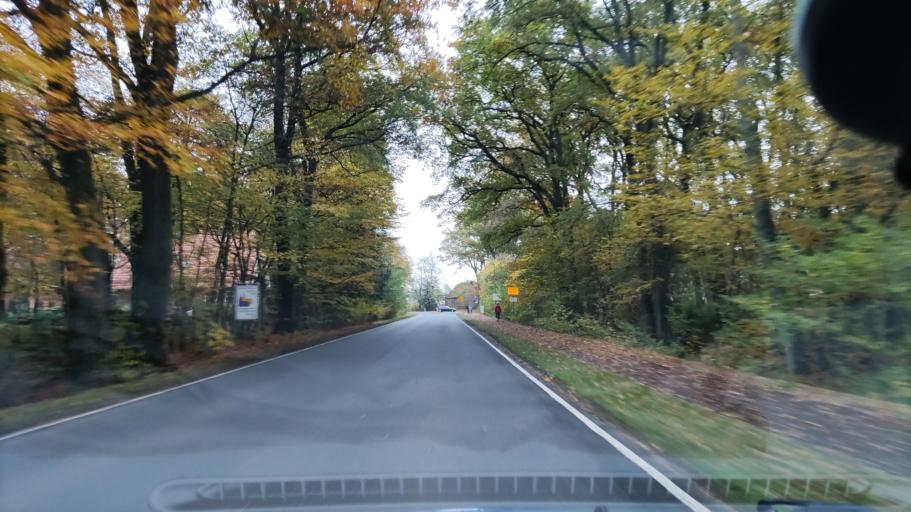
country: DE
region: Lower Saxony
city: Munster
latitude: 53.0156
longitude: 10.0841
